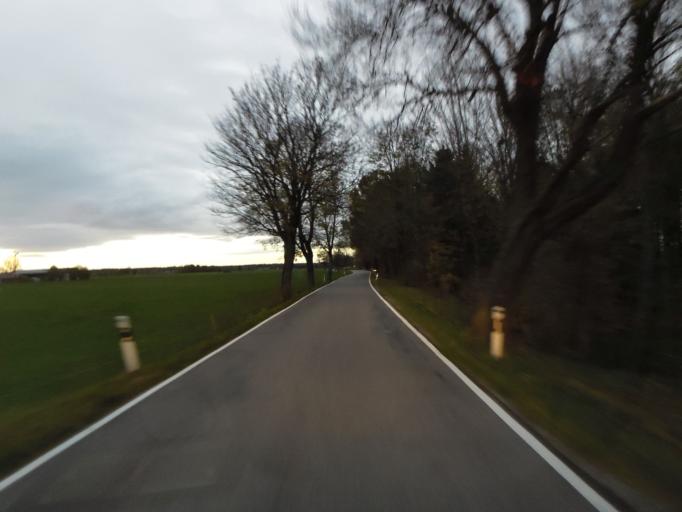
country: DE
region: Bavaria
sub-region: Upper Bavaria
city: Valley
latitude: 47.8761
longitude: 11.7830
